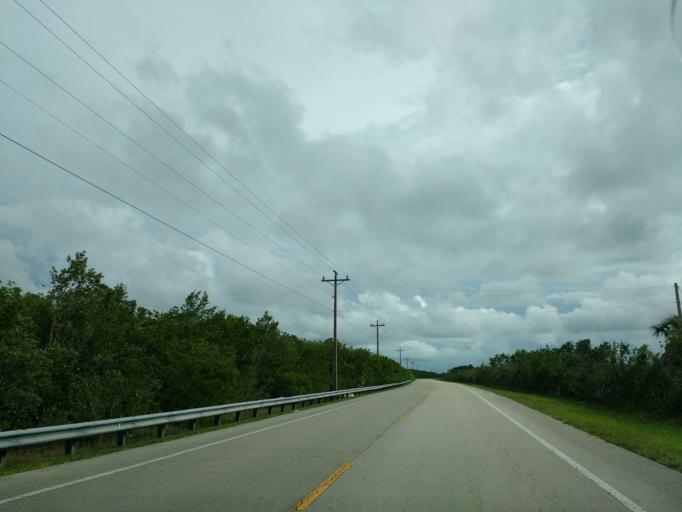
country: US
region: Florida
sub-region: Collier County
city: Marco
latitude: 25.8850
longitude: -81.3781
